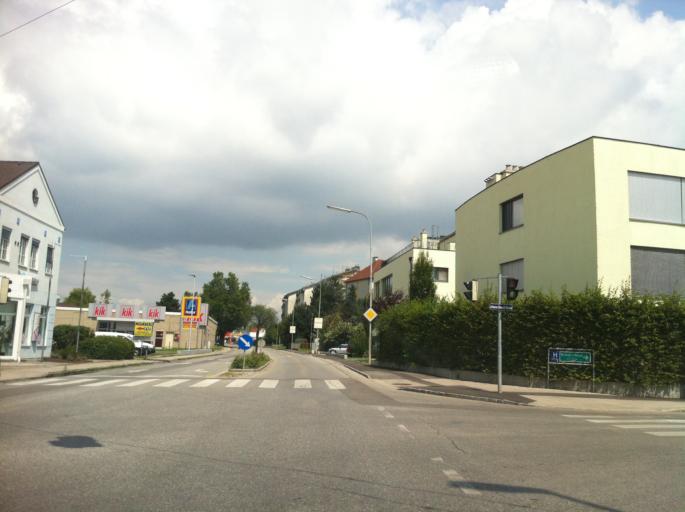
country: AT
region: Lower Austria
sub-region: Politischer Bezirk Tulln
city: Tulln
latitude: 48.3230
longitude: 16.0587
